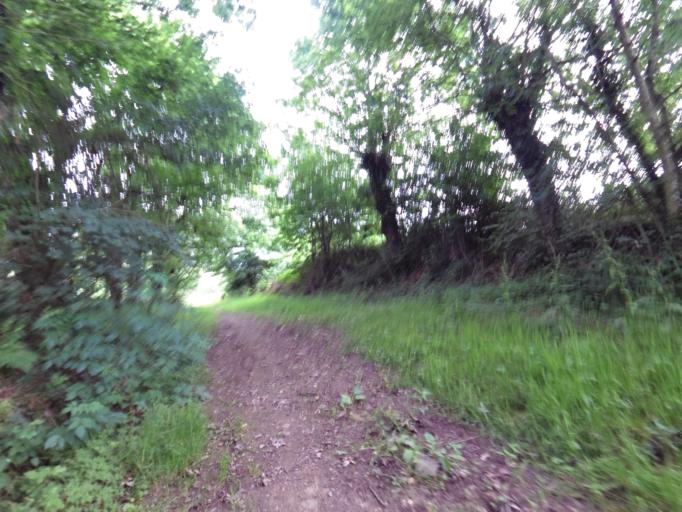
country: FR
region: Brittany
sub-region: Departement d'Ille-et-Vilaine
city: Crevin
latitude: 47.9296
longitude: -1.6287
